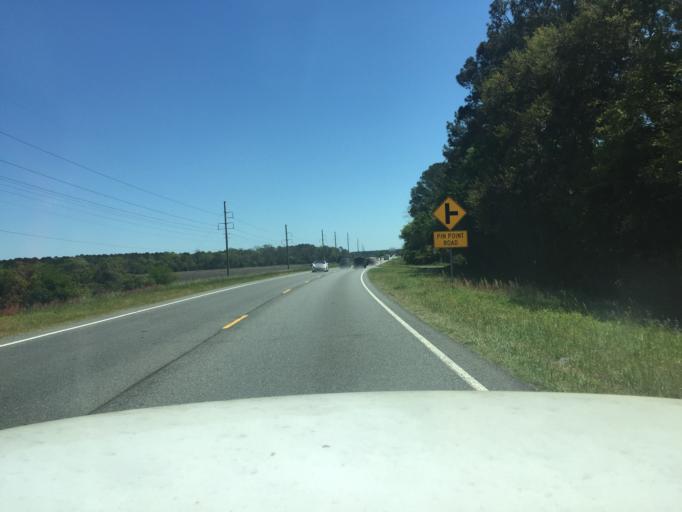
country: US
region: Georgia
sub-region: Chatham County
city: Montgomery
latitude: 31.9547
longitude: -81.0909
